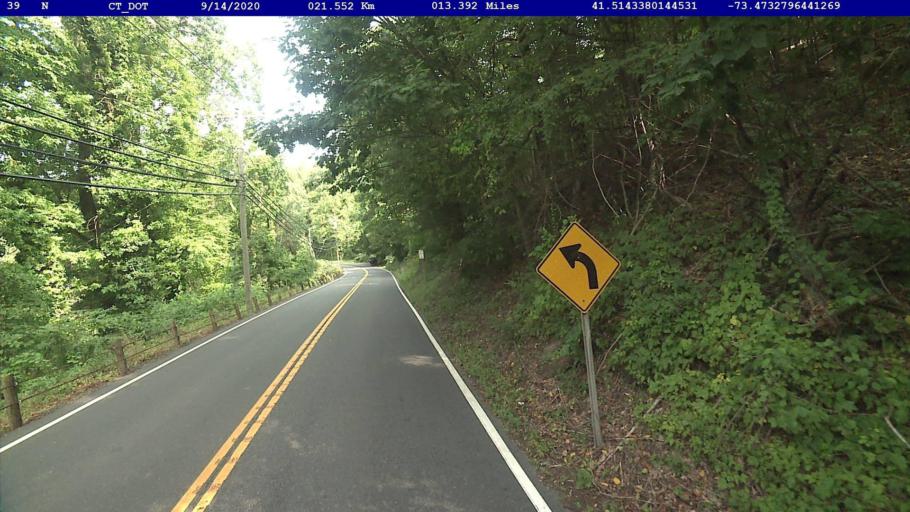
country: US
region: Connecticut
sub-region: Fairfield County
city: Sherman
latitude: 41.5143
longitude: -73.4733
